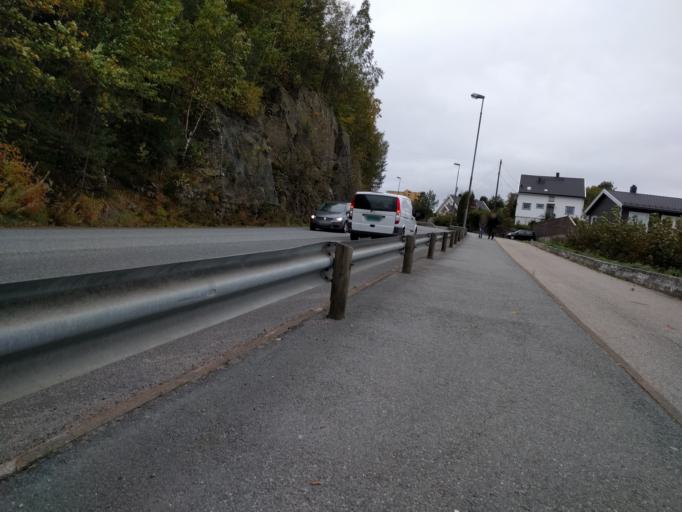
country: NO
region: Vest-Agder
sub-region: Kristiansand
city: Kristiansand
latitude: 58.1459
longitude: 7.9714
